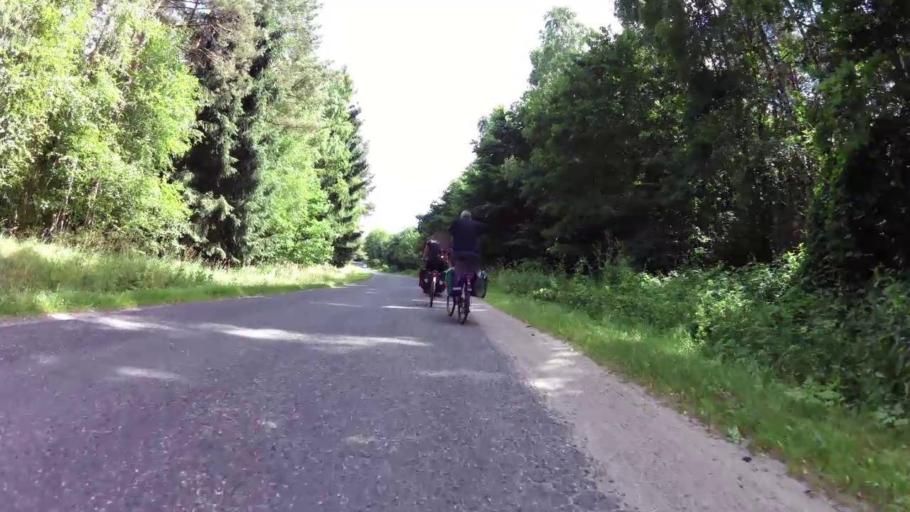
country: PL
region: West Pomeranian Voivodeship
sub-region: Powiat lobeski
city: Lobez
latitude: 53.6642
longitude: 15.5527
